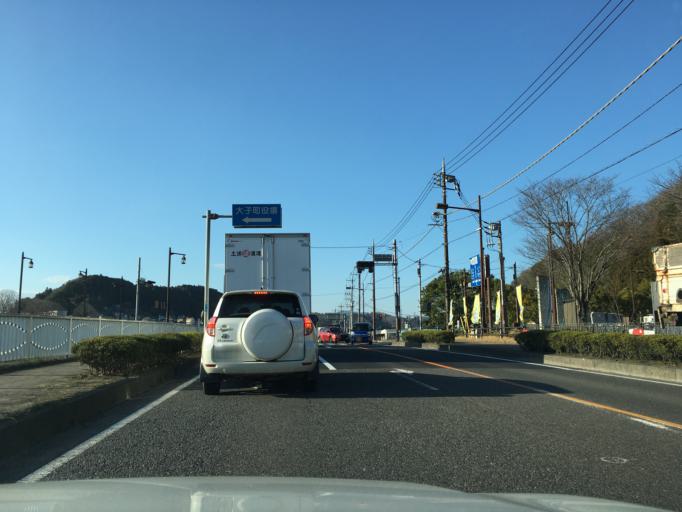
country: JP
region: Ibaraki
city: Daigo
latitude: 36.7682
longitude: 140.3587
